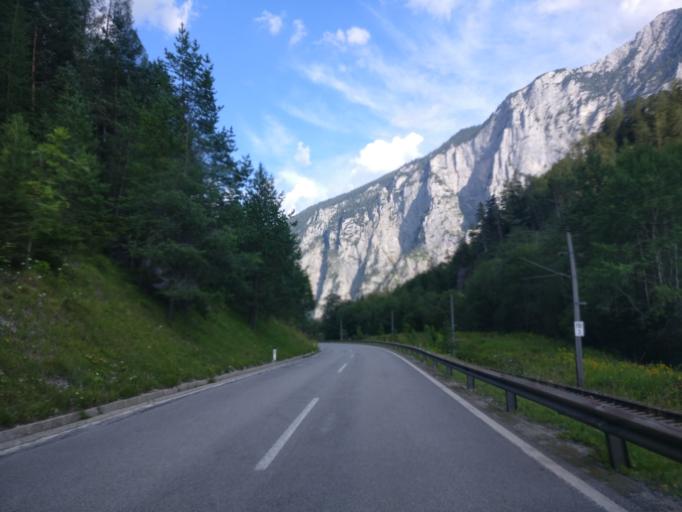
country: AT
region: Styria
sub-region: Politischer Bezirk Liezen
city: Johnsbach
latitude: 47.5916
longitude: 14.6467
